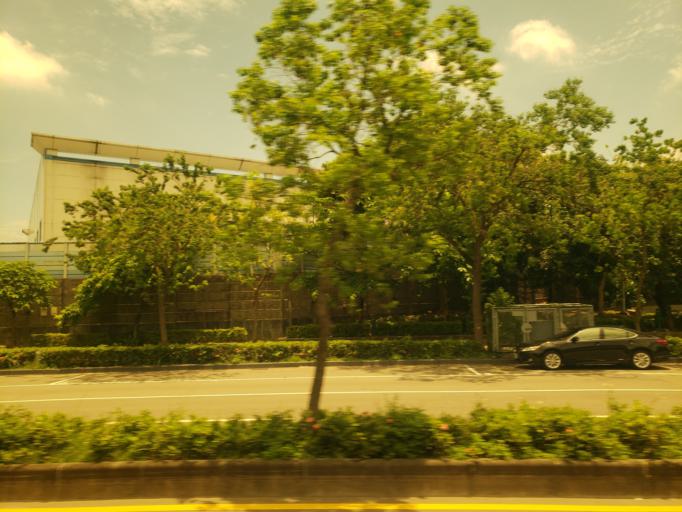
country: TW
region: Taipei
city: Taipei
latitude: 25.0579
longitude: 121.6204
